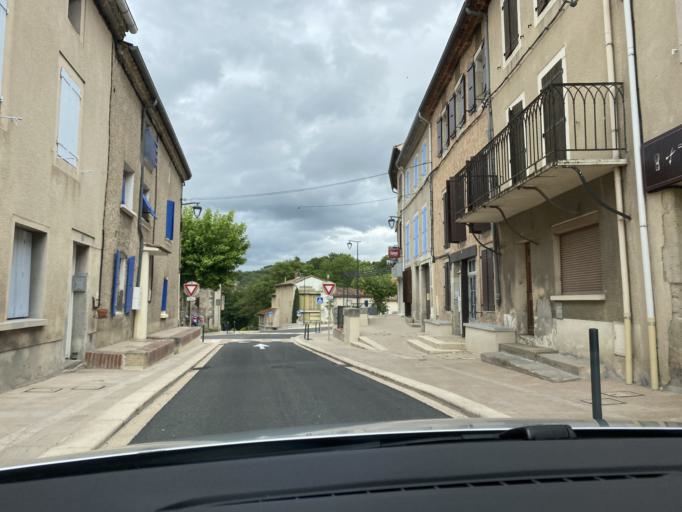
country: FR
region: Midi-Pyrenees
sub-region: Departement du Tarn
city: Saix
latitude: 43.5818
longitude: 2.1836
